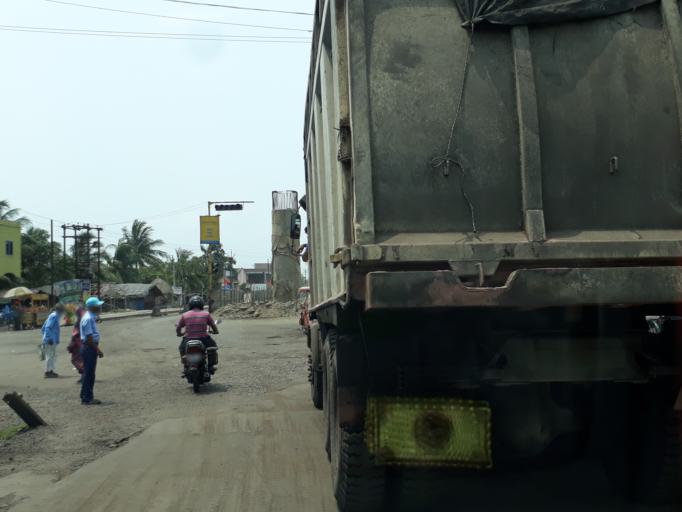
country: IN
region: West Bengal
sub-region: Purba Medinipur
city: Haldia
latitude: 22.0526
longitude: 88.0866
